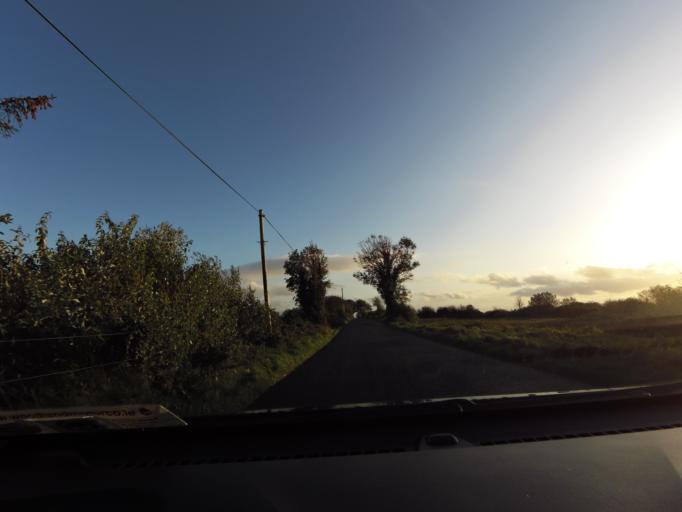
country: IE
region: Connaught
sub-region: Roscommon
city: Castlerea
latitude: 53.6668
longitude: -8.5970
